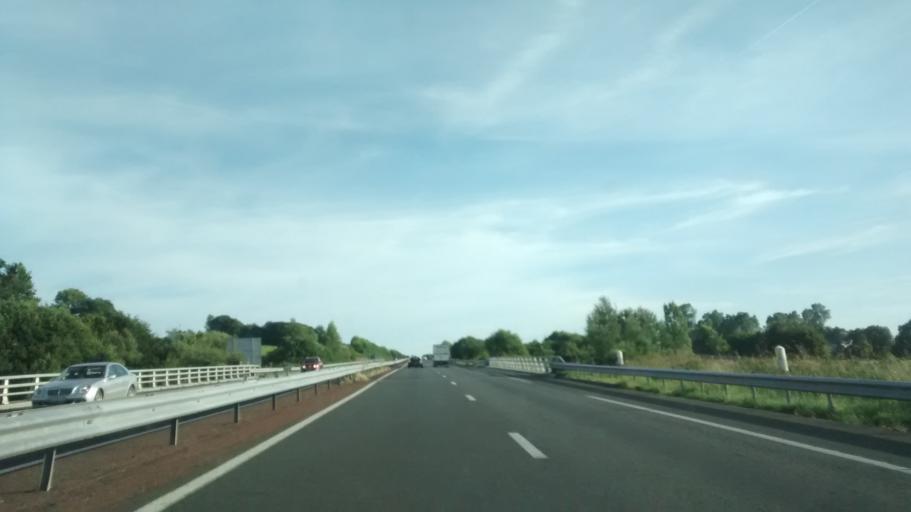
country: FR
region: Lower Normandy
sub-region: Departement de la Manche
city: Villedieu-les-Poeles
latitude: 48.7953
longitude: -1.2644
